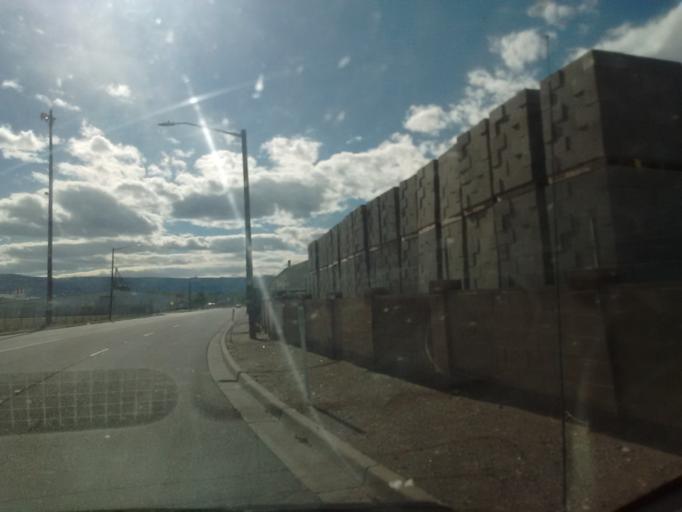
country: US
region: Colorado
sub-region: Mesa County
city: Grand Junction
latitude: 39.0617
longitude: -108.5545
